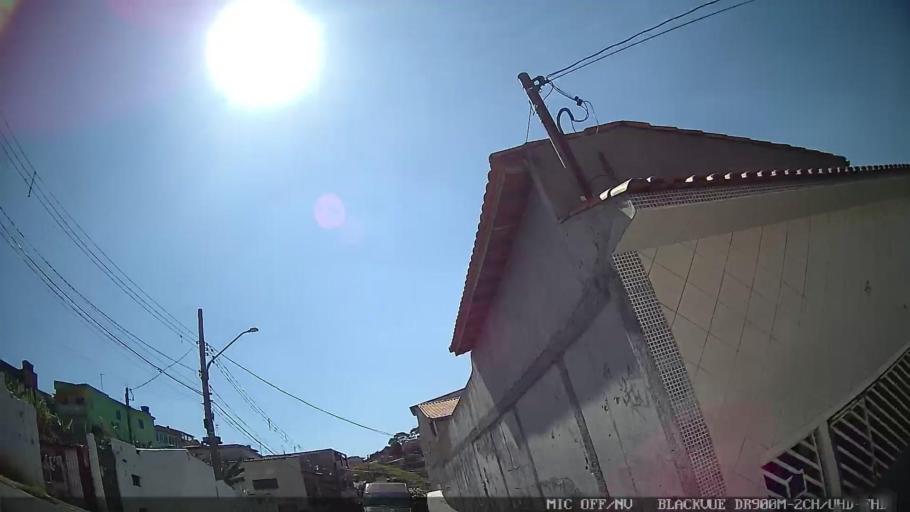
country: BR
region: Sao Paulo
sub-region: Sao Caetano Do Sul
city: Sao Caetano do Sul
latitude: -23.5921
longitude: -46.4972
